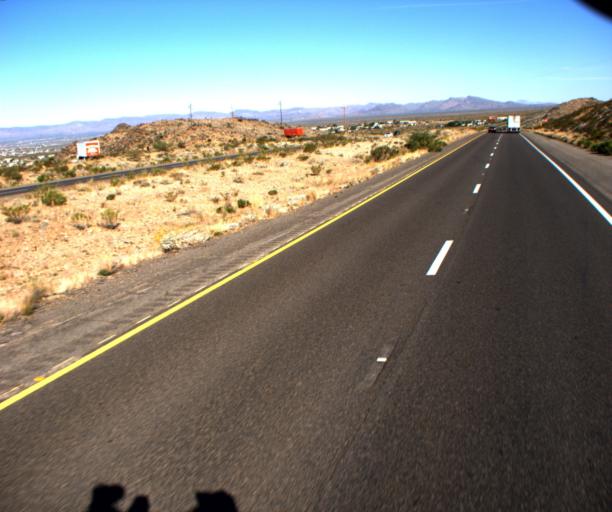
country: US
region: Arizona
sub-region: Mohave County
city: Golden Valley
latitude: 35.2350
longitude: -114.1394
